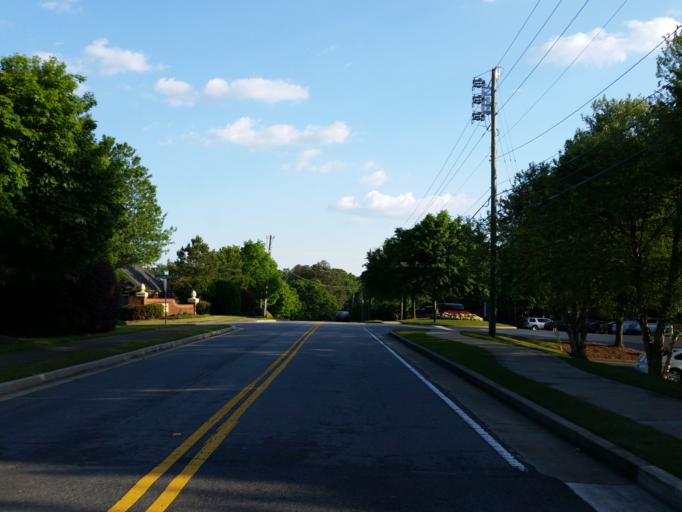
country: US
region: Georgia
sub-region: Cobb County
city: Marietta
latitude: 33.9740
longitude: -84.4777
